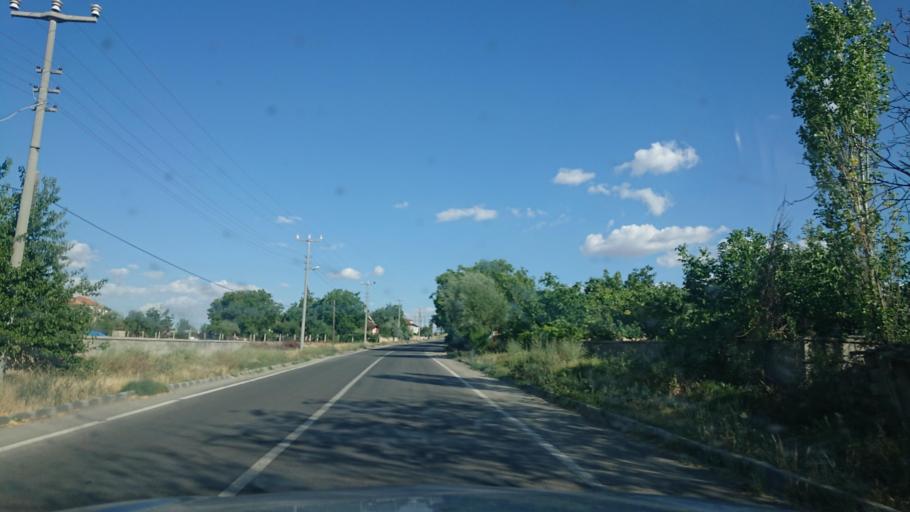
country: TR
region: Aksaray
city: Sariyahsi
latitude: 38.9879
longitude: 33.8513
